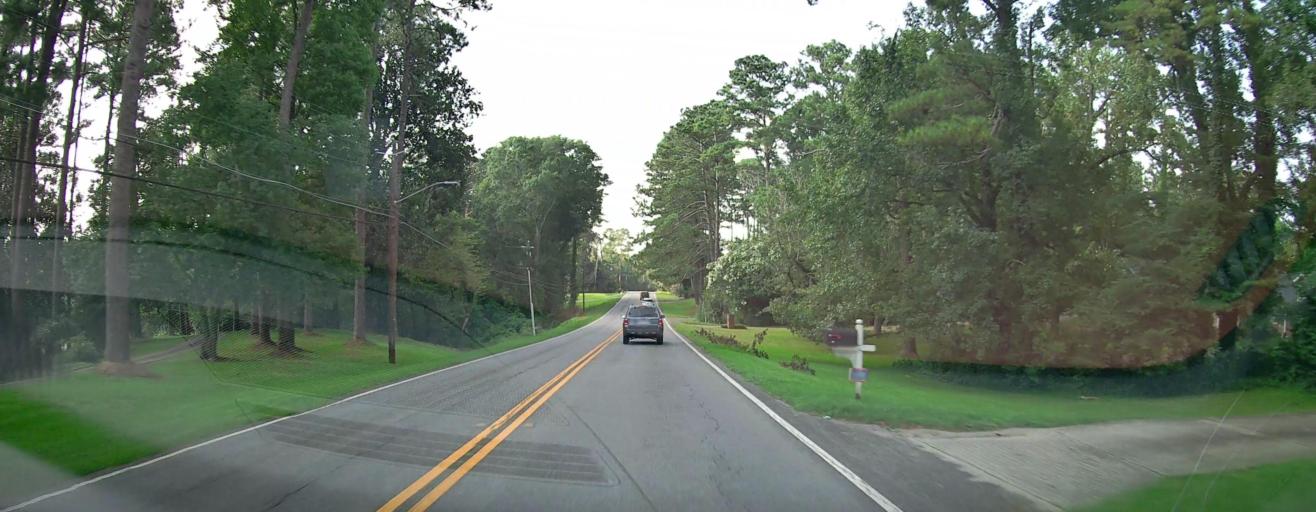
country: US
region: Georgia
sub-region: Bibb County
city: Macon
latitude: 32.8551
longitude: -83.6624
